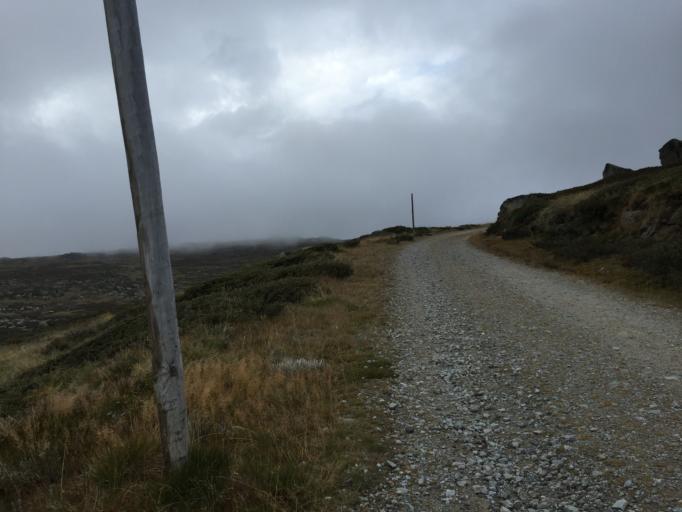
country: AU
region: New South Wales
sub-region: Snowy River
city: Jindabyne
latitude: -36.4557
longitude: 148.3018
